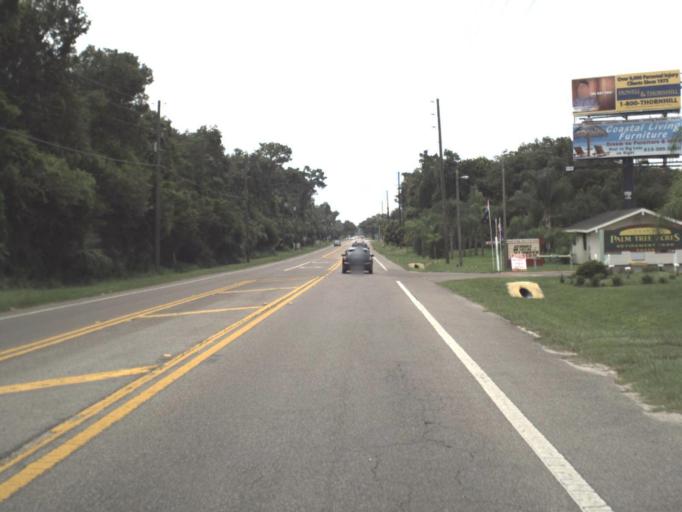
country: US
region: Florida
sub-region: Pasco County
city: Zephyrhills West
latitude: 28.2299
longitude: -82.2211
